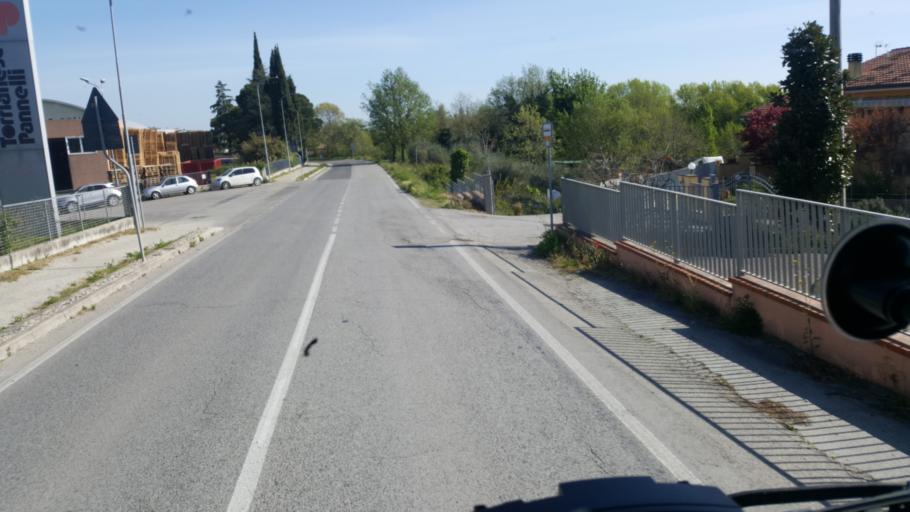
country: IT
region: Emilia-Romagna
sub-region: Provincia di Rimini
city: Torriana
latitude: 43.9943
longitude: 12.4018
